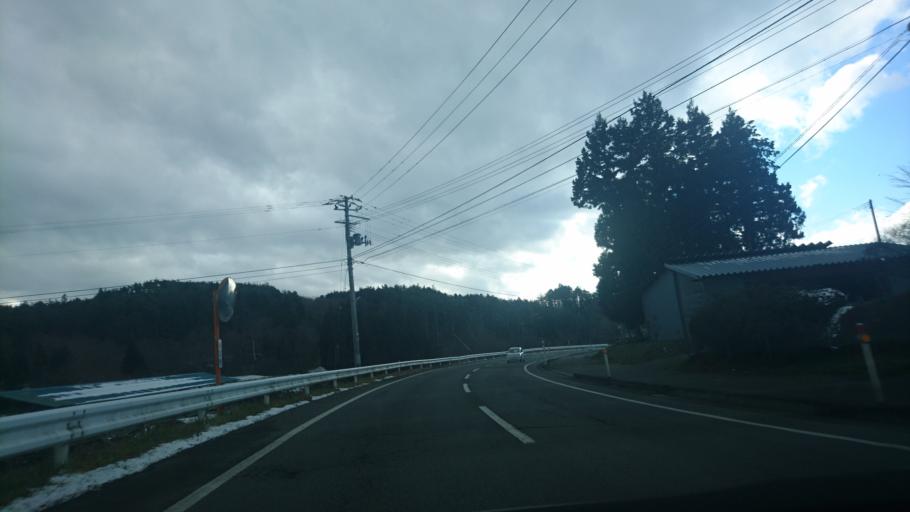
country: JP
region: Iwate
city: Mizusawa
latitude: 39.1465
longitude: 141.2089
